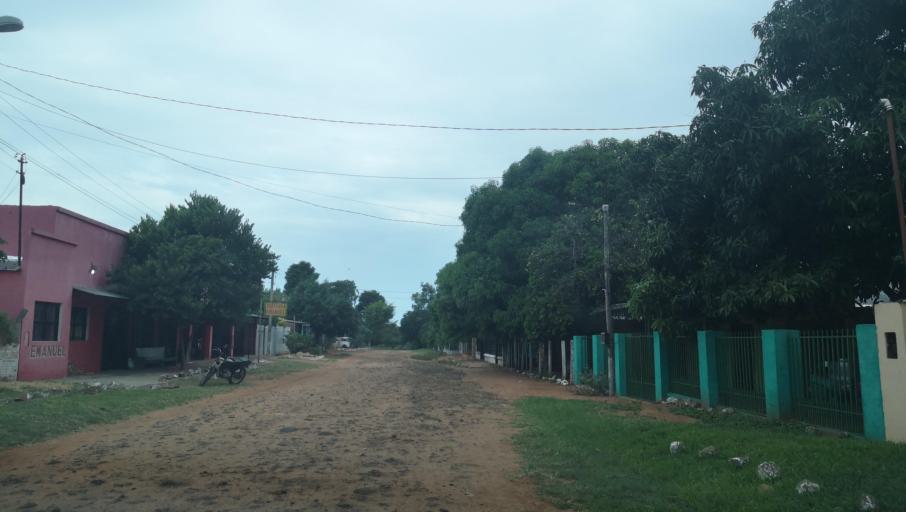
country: PY
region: San Pedro
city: Capiibary
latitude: -24.7272
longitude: -56.0134
